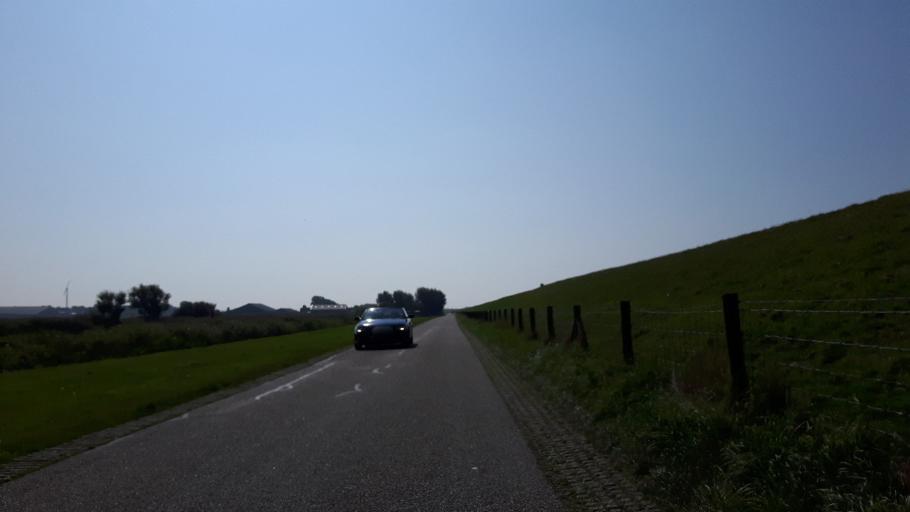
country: NL
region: Friesland
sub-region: Sudwest Fryslan
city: Makkum
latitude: 53.0907
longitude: 5.3806
